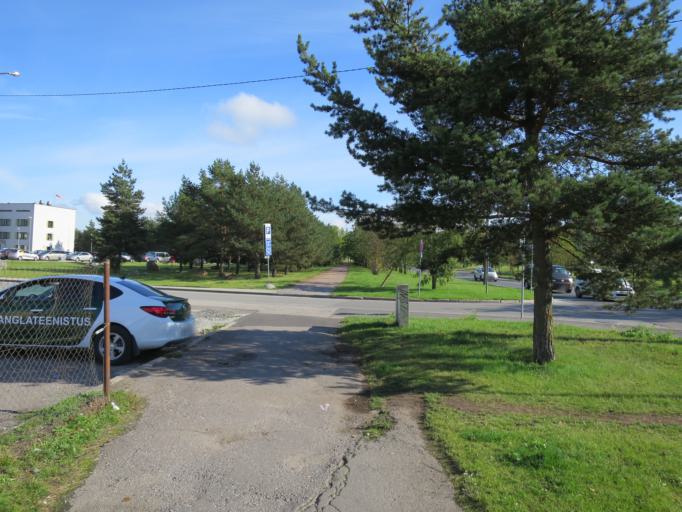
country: EE
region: Harju
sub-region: Tallinna linn
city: Tallinn
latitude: 59.3968
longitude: 24.6998
